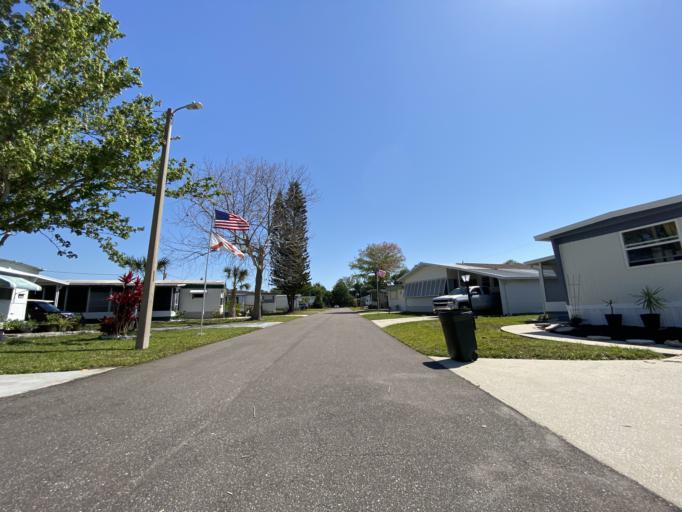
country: US
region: Florida
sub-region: Volusia County
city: South Daytona
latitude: 29.1568
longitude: -81.0172
